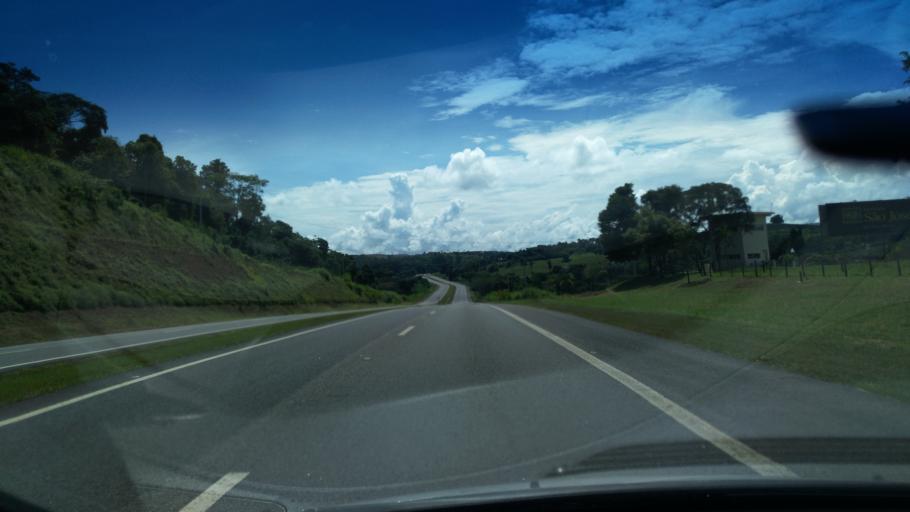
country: BR
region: Sao Paulo
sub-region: Santo Antonio Do Jardim
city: Espirito Santo do Pinhal
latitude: -22.2357
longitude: -46.7983
